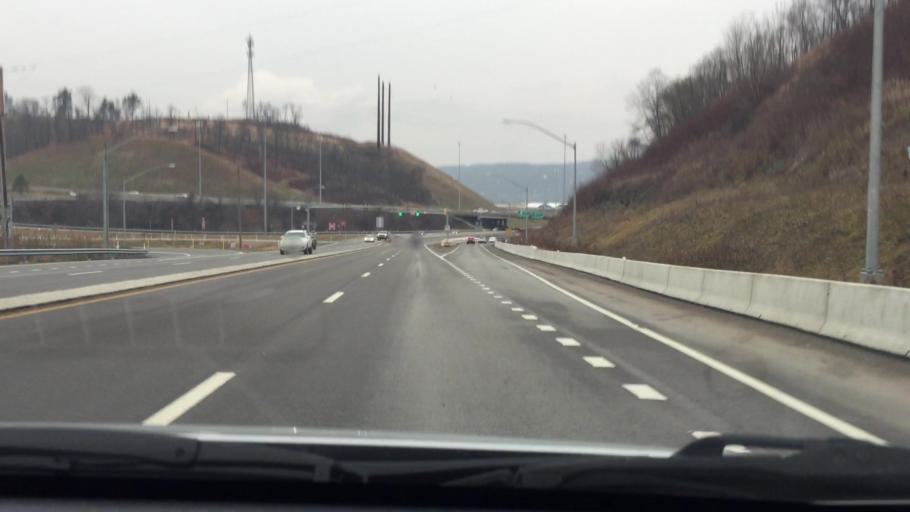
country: US
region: Pennsylvania
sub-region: Beaver County
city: Beaver
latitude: 40.6684
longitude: -80.3202
